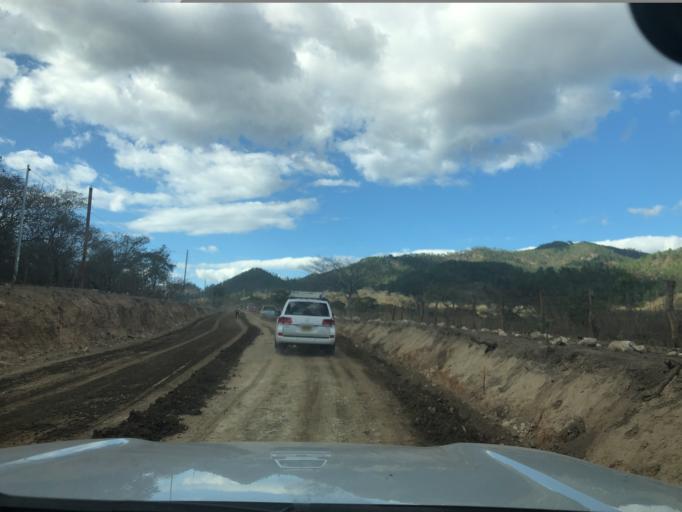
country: NI
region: Nueva Segovia
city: Ocotal
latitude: 13.6612
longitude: -86.6133
